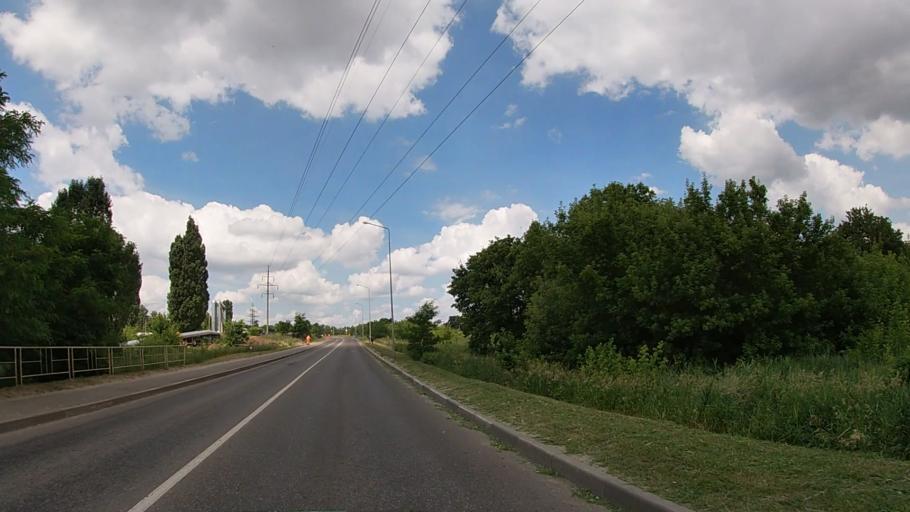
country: RU
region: Belgorod
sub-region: Belgorodskiy Rayon
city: Belgorod
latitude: 50.5925
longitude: 36.5616
